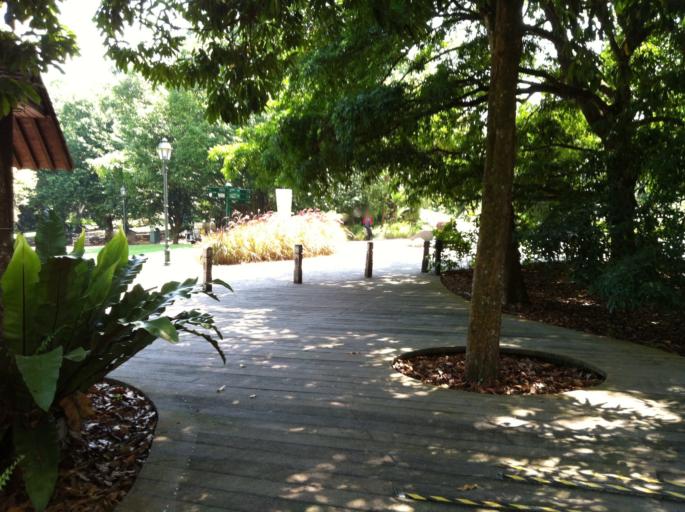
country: SG
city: Singapore
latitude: 1.3091
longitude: 103.8173
